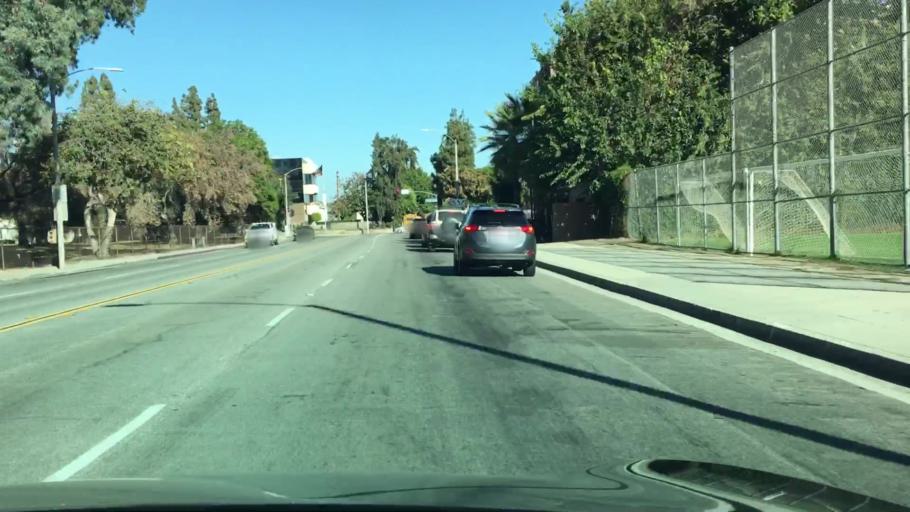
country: US
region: California
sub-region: Los Angeles County
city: Arcadia
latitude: 34.1308
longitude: -118.0328
